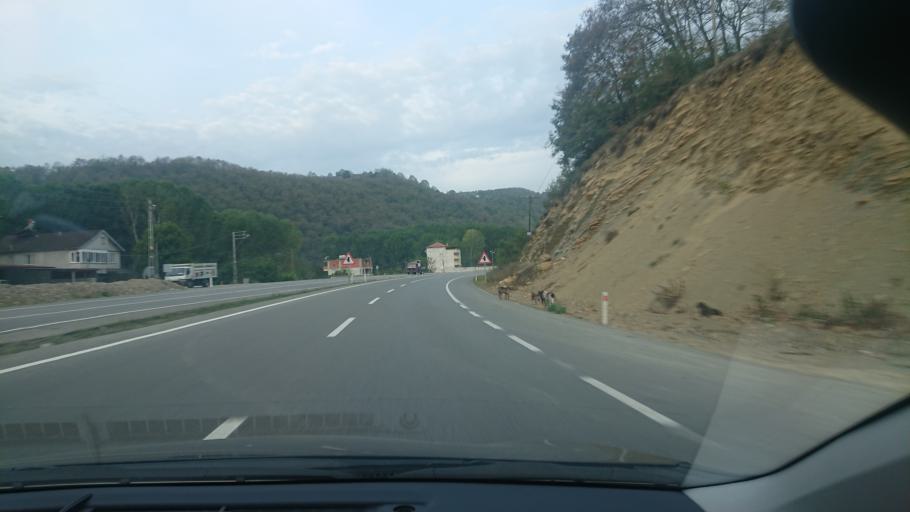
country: TR
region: Zonguldak
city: Beycuma
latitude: 41.3242
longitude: 32.0508
